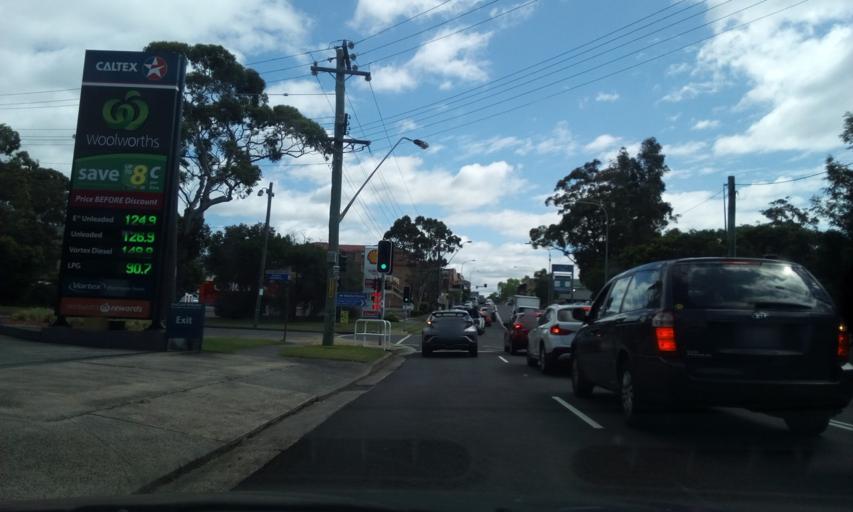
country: AU
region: New South Wales
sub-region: Wollongong
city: Corrimal
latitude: -34.3753
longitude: 150.8965
